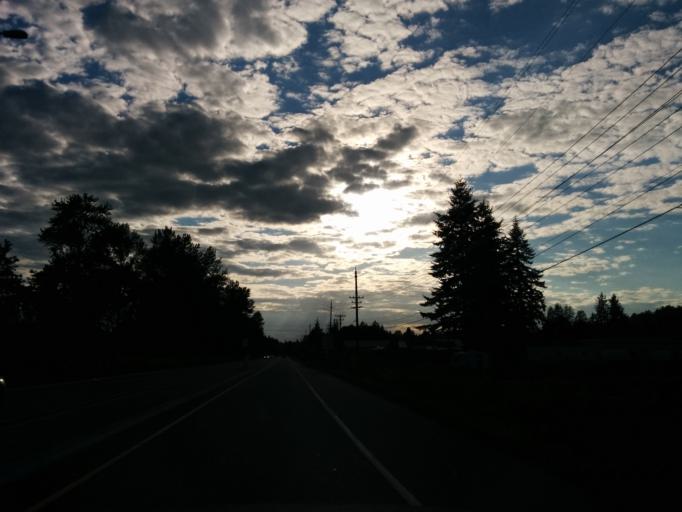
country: US
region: Washington
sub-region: Snohomish County
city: Sultan
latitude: 47.8678
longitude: -121.7790
